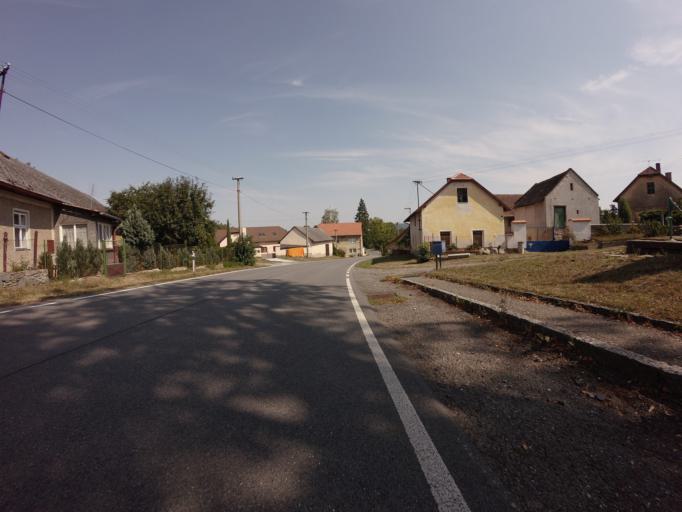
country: CZ
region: Central Bohemia
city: Sedlcany
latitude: 49.6261
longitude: 14.4244
